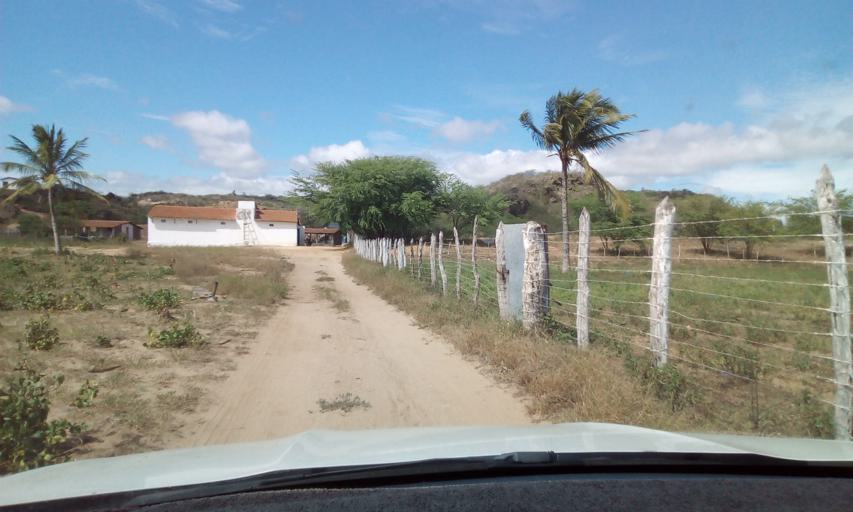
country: BR
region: Paraiba
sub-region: Picui
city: Picui
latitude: -6.5143
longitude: -36.3523
